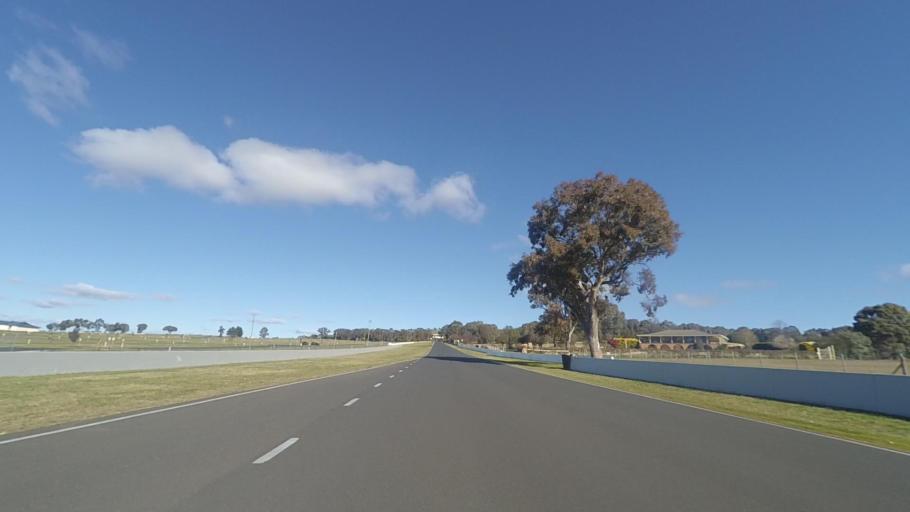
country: AU
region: New South Wales
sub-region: Bathurst Regional
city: Bathurst
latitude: -33.4400
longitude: 149.5552
